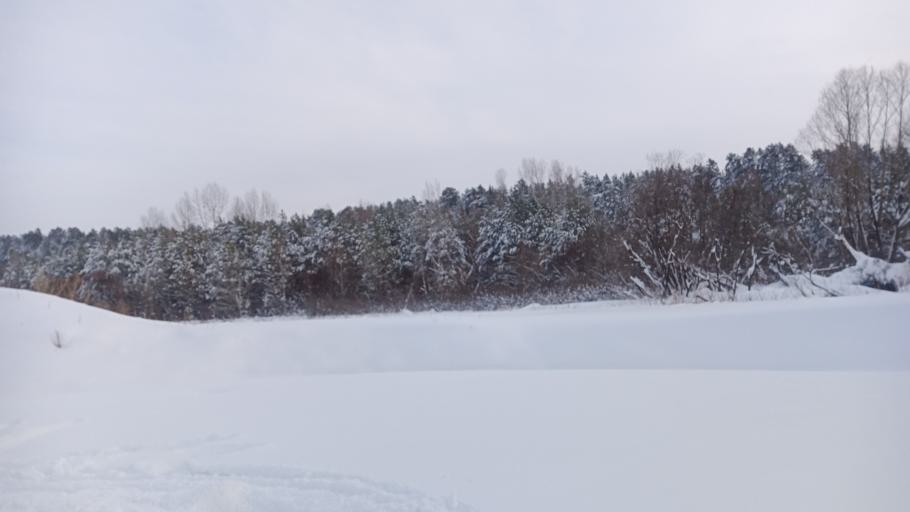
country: RU
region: Altai Krai
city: Yuzhnyy
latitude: 53.3070
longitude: 83.7179
